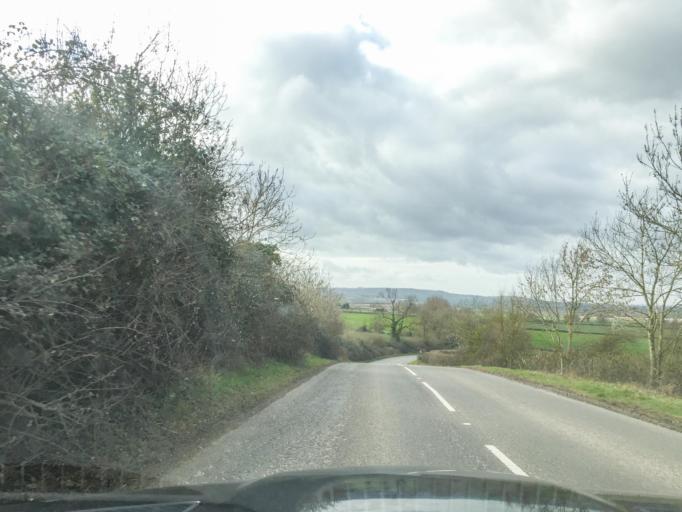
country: GB
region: England
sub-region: Warwickshire
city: Shipston on Stour
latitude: 52.0598
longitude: -1.5640
